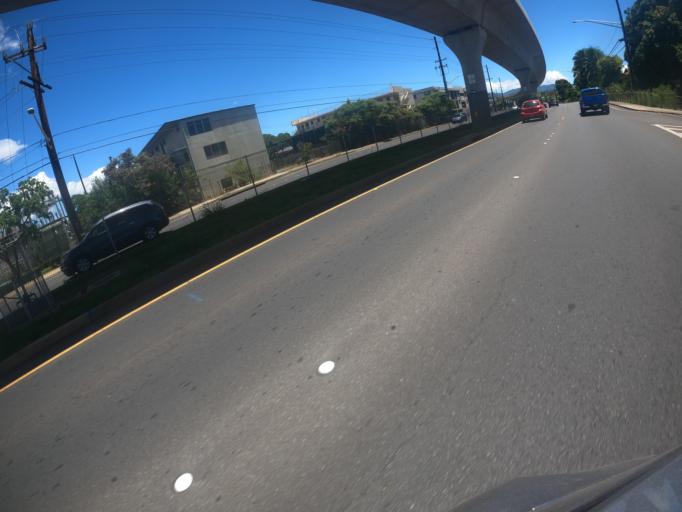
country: US
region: Hawaii
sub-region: Honolulu County
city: Waipahu
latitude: 21.3849
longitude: -158.0004
